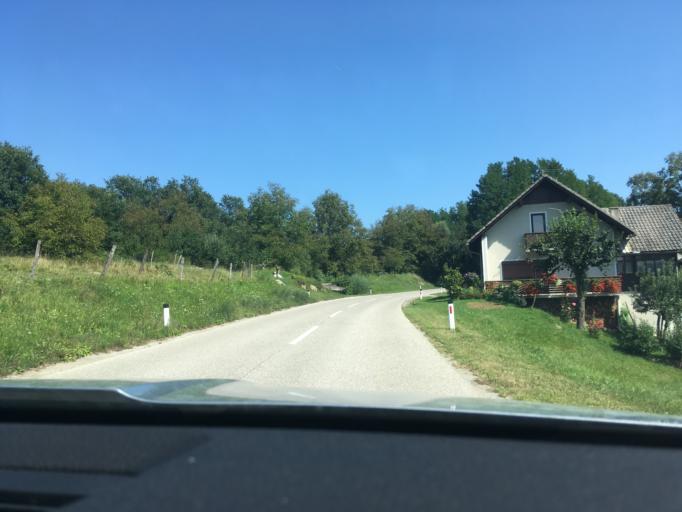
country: SI
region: Metlika
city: Metlika
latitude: 45.5329
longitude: 15.3001
